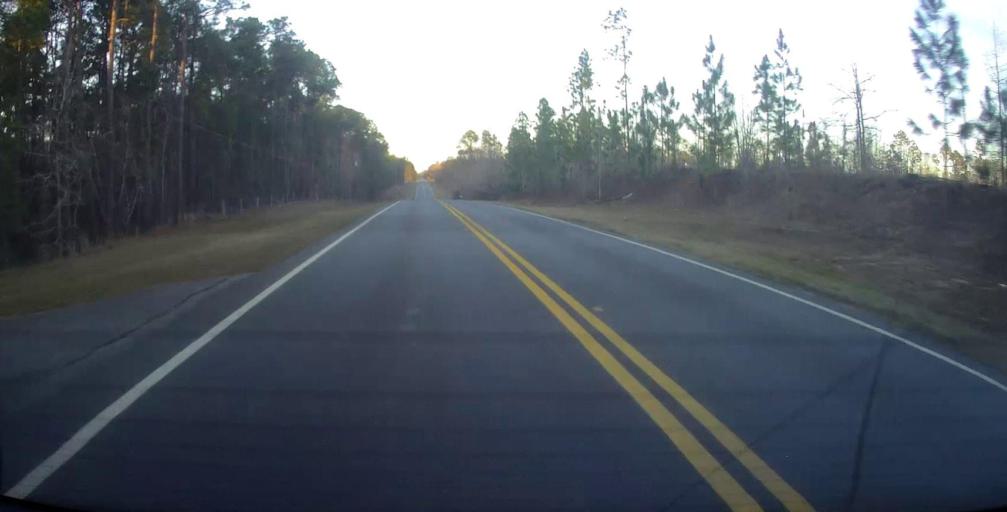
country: US
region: Georgia
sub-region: Dodge County
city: Chester
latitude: 32.3249
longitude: -83.0506
